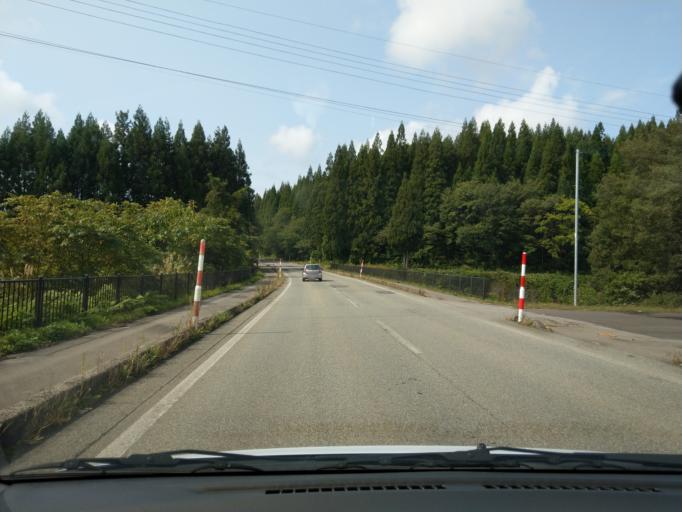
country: JP
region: Akita
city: Omagari
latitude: 39.4421
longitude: 140.3427
